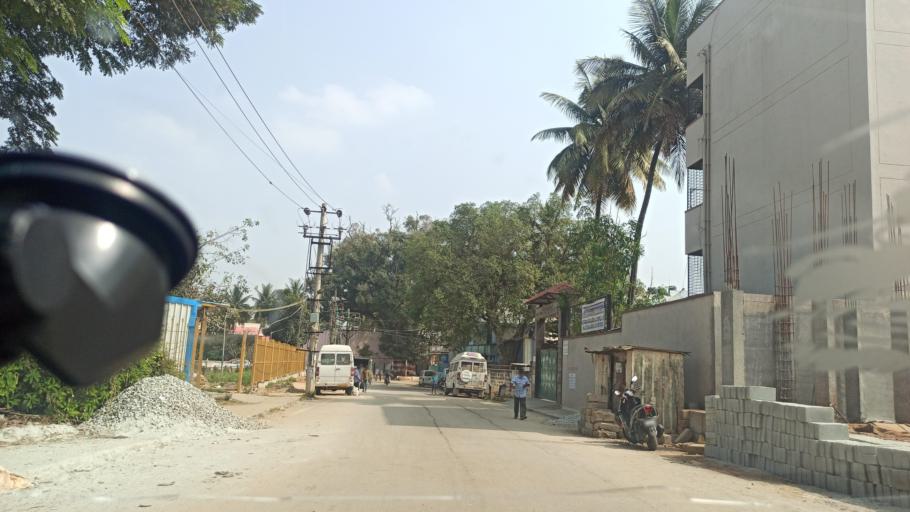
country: IN
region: Karnataka
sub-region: Bangalore Urban
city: Yelahanka
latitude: 13.1041
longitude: 77.5959
